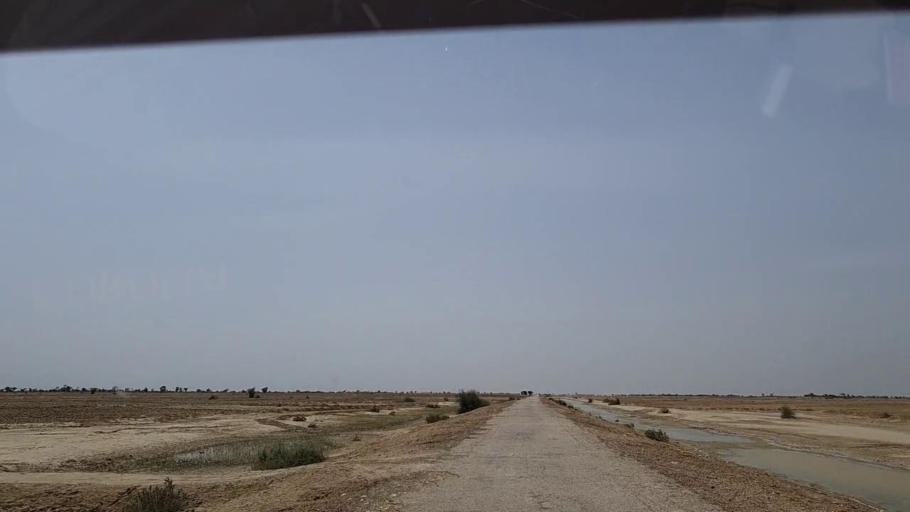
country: PK
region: Sindh
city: Johi
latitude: 26.7242
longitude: 67.6428
